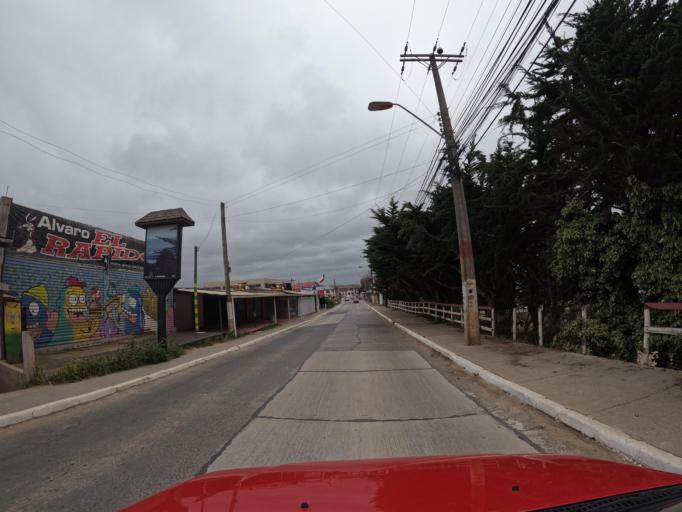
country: CL
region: O'Higgins
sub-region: Provincia de Colchagua
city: Santa Cruz
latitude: -34.3870
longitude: -72.0092
